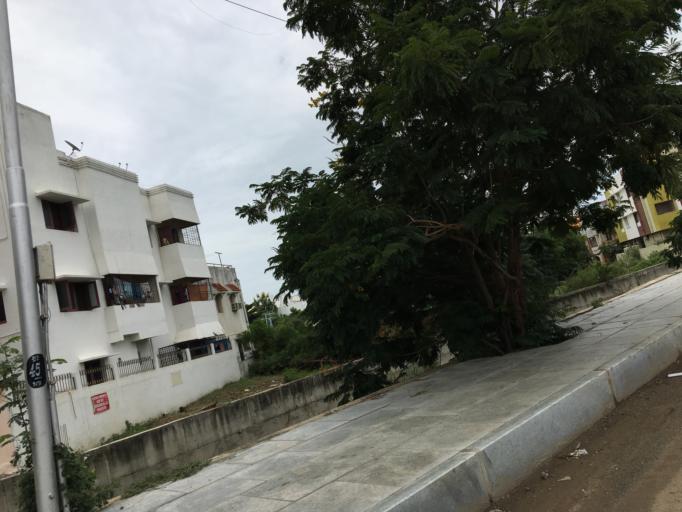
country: IN
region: Tamil Nadu
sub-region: Kancheepuram
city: Madipakkam
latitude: 12.9708
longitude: 80.2137
